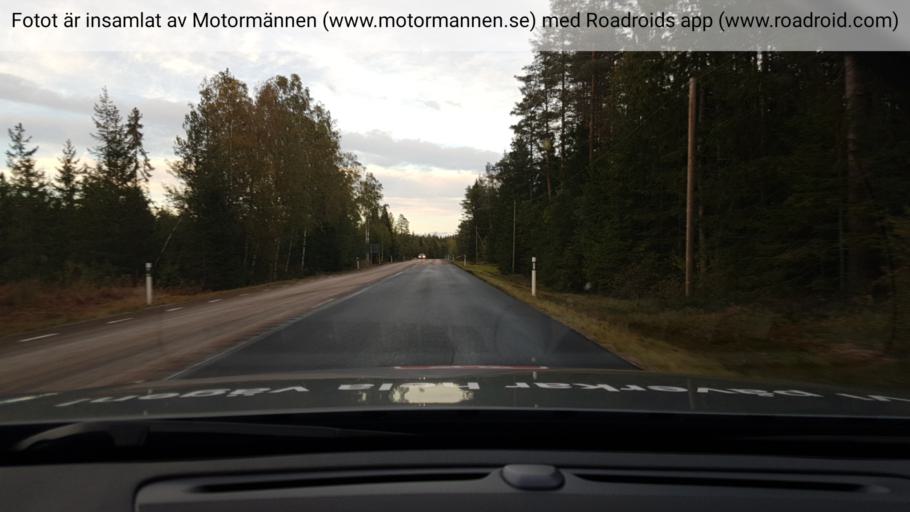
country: SE
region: Vaestra Goetaland
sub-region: Amals Kommun
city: Amal
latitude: 59.0719
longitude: 12.5629
